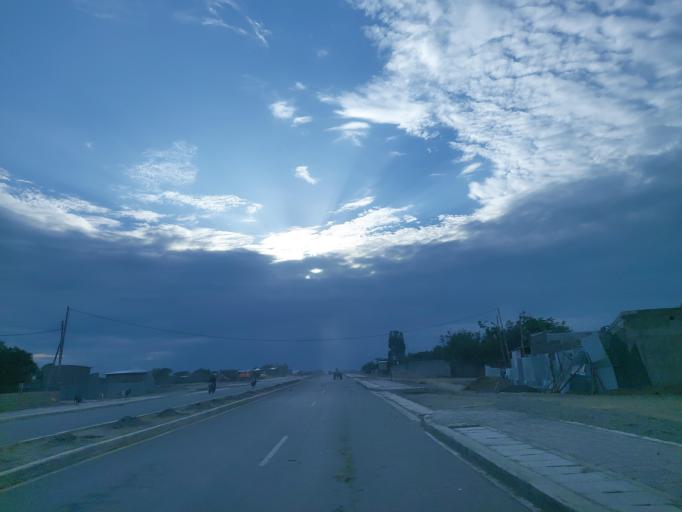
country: ET
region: Oromiya
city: Ziway
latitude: 8.1459
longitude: 38.8065
